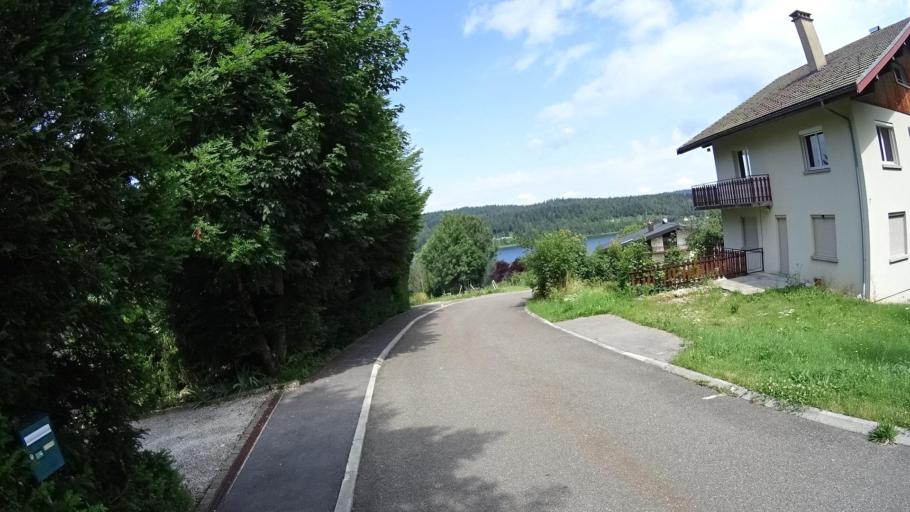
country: FR
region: Franche-Comte
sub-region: Departement du Doubs
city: Les Fourgs
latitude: 46.8270
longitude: 6.3336
